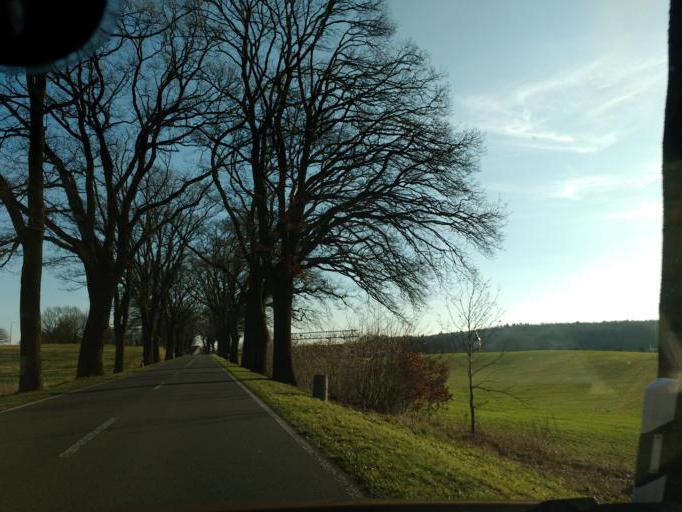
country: DE
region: Brandenburg
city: Protzel
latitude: 52.6391
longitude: 13.9800
